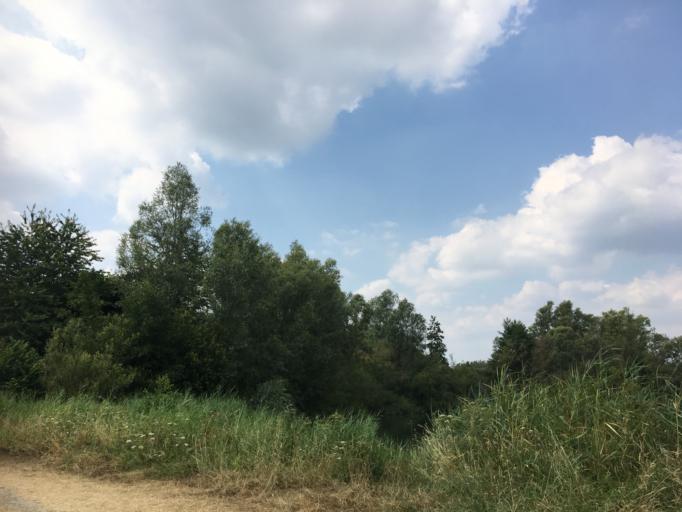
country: NL
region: Gelderland
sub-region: Gemeente Buren
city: Lienden
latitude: 51.9542
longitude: 5.5395
